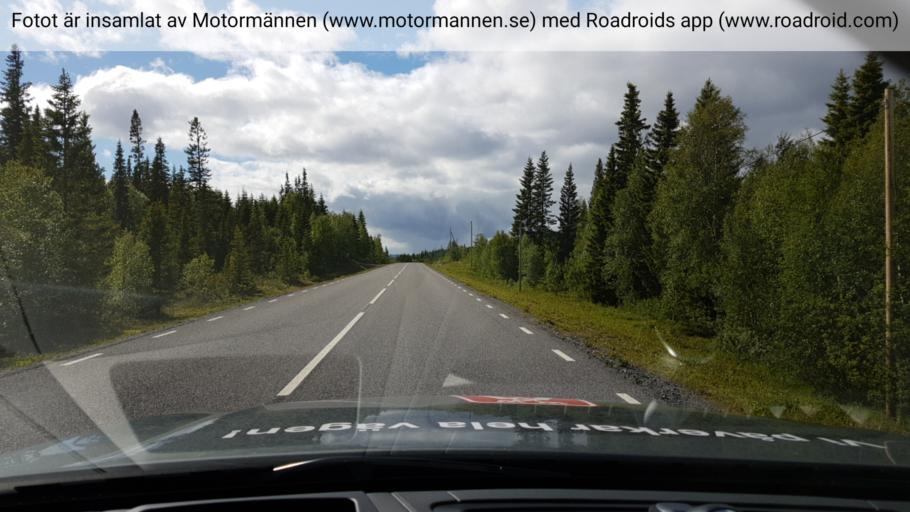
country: SE
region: Jaemtland
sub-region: Are Kommun
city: Are
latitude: 63.6195
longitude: 13.1752
